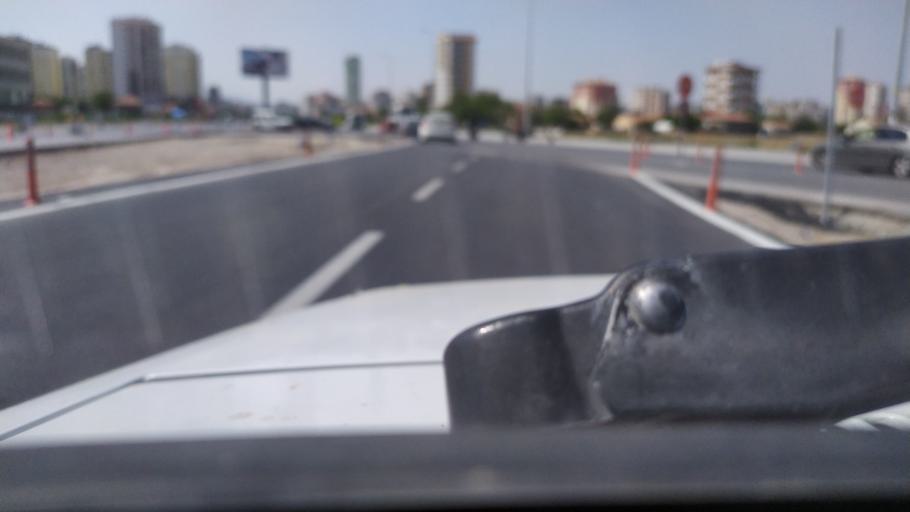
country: TR
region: Kayseri
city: Talas
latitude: 38.7202
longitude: 35.5474
